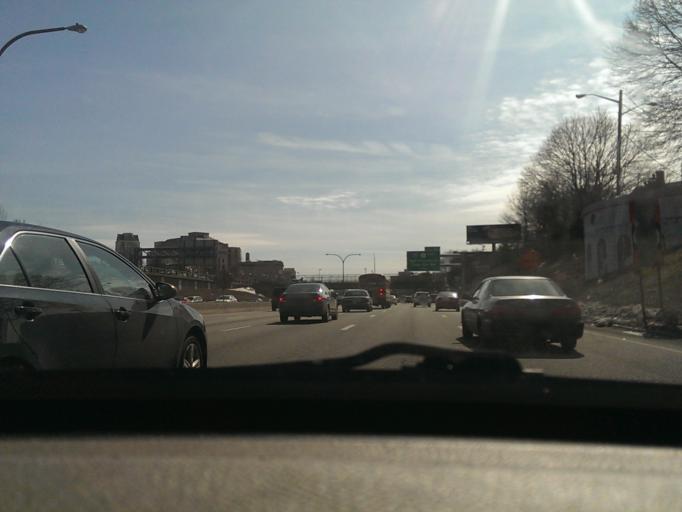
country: US
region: Rhode Island
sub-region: Providence County
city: Providence
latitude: 41.8338
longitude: -71.4166
